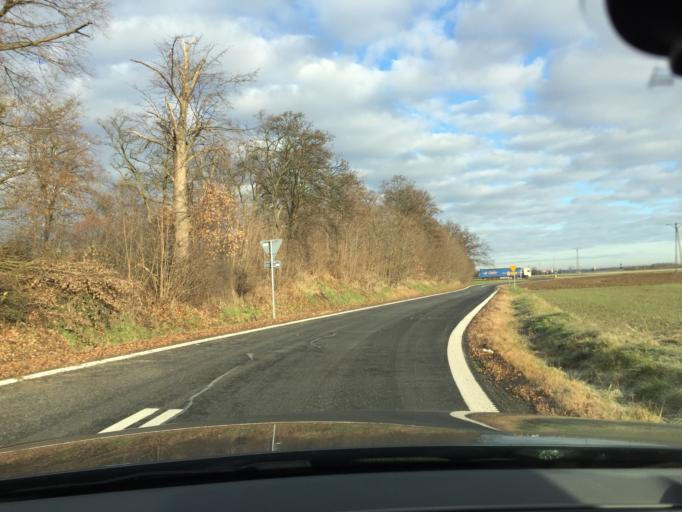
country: PL
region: Lower Silesian Voivodeship
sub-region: Powiat sredzki
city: Udanin
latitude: 51.0580
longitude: 16.5208
